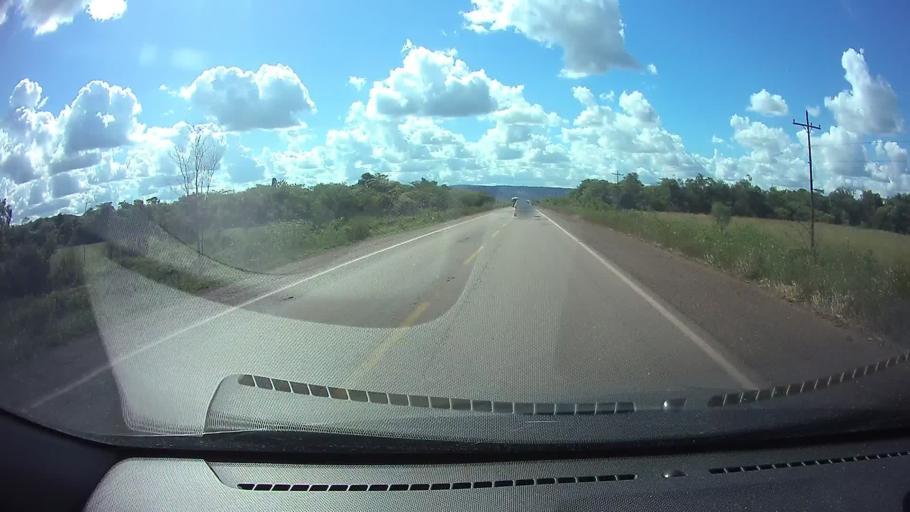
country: PY
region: Paraguari
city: Sapucai
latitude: -25.7177
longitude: -56.8339
